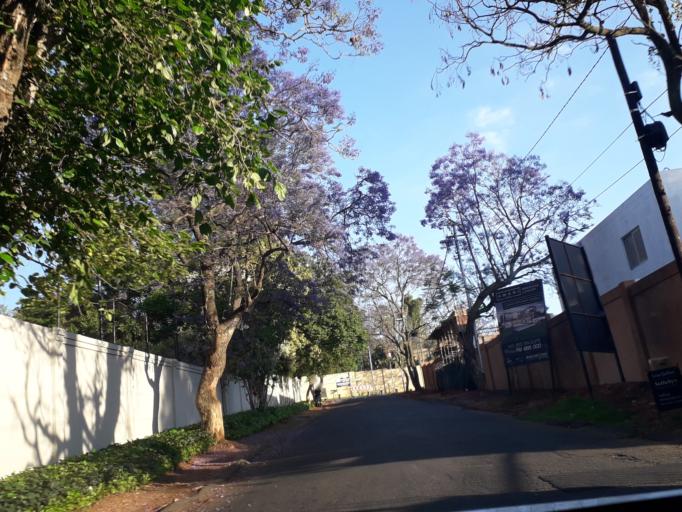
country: ZA
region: Gauteng
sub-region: City of Johannesburg Metropolitan Municipality
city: Johannesburg
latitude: -26.1164
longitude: 28.0642
